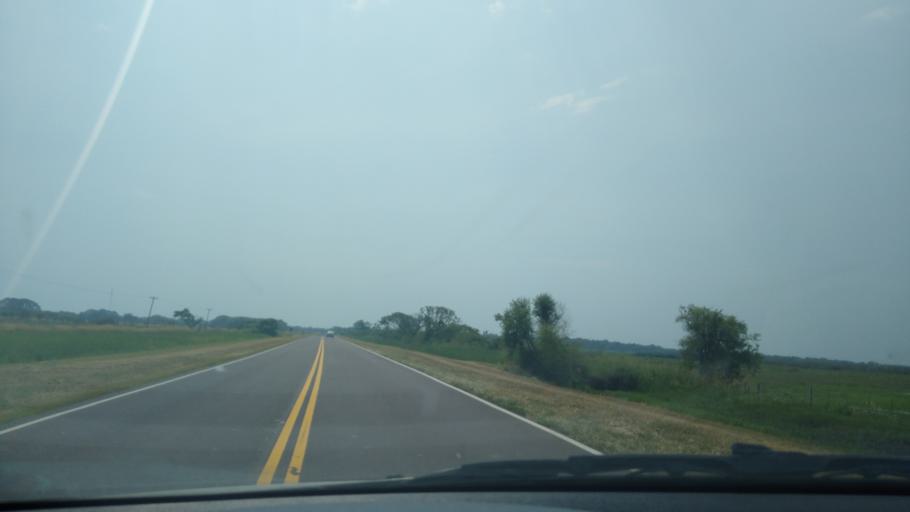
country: AR
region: Chaco
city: La Eduvigis
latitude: -26.8500
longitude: -59.0479
